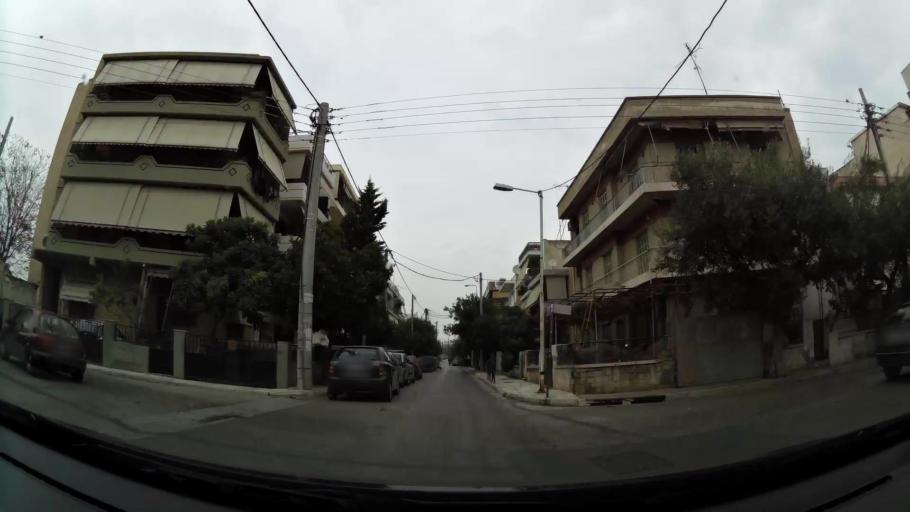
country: GR
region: Attica
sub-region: Nomos Piraios
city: Agios Ioannis Rentis
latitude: 37.9616
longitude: 23.6715
